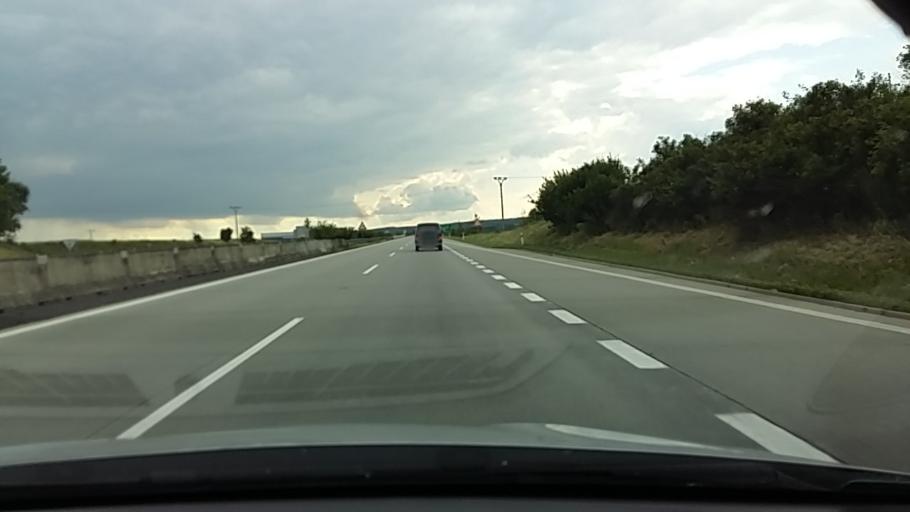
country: CZ
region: Plzensky
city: Hermanova Hut'
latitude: 49.7163
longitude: 13.1327
